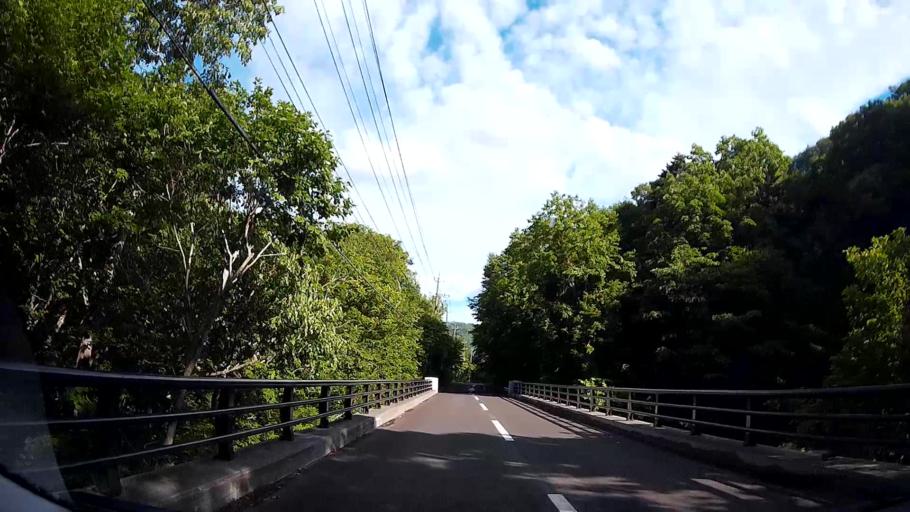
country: JP
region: Hokkaido
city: Sapporo
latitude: 42.9815
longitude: 141.1597
